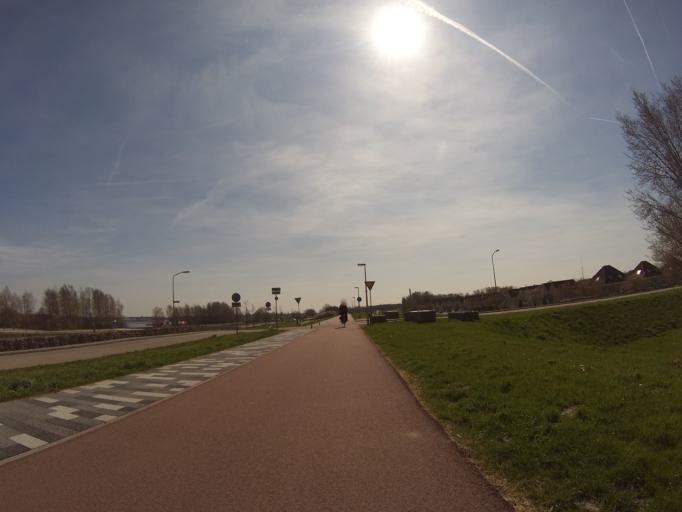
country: NL
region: Flevoland
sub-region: Gemeente Zeewolde
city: Zeewolde
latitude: 52.3248
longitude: 5.5480
